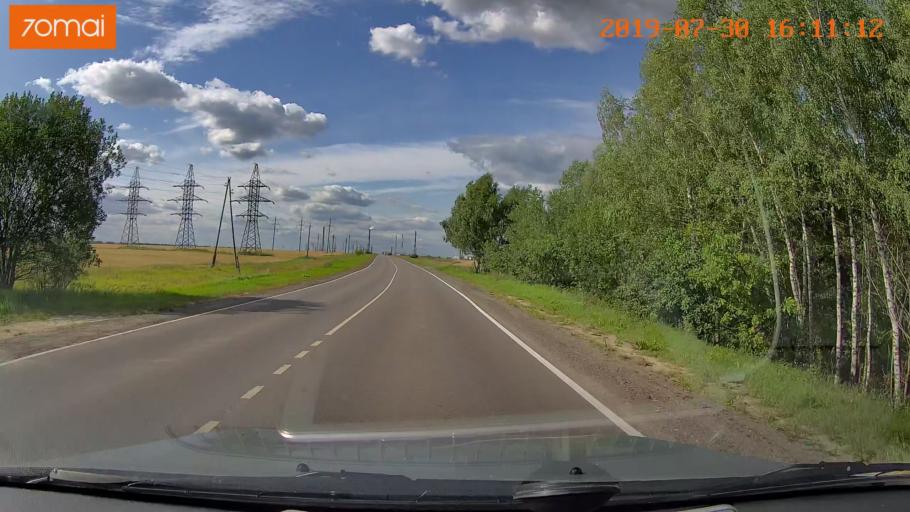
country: RU
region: Moskovskaya
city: Lopatinskiy
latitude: 55.2724
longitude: 38.7132
